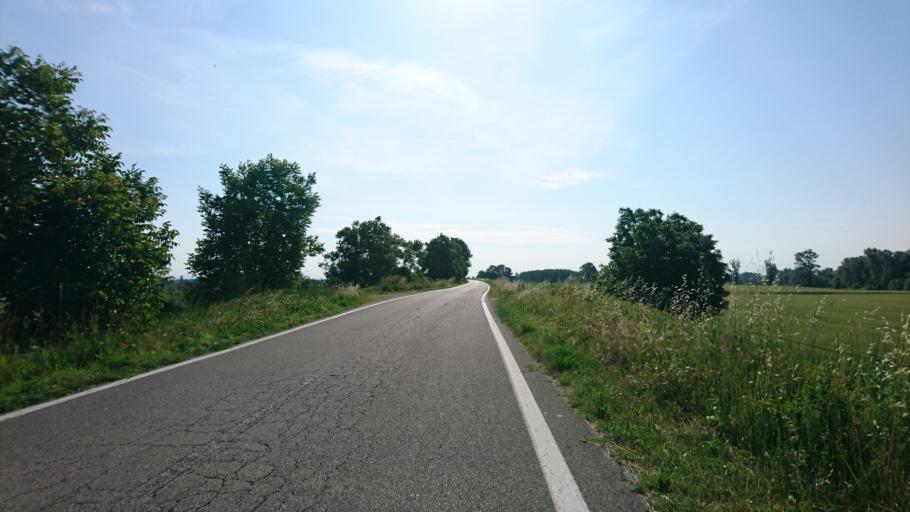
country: IT
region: Veneto
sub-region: Provincia di Verona
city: Villa Bartolomea
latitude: 45.1660
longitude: 11.3579
